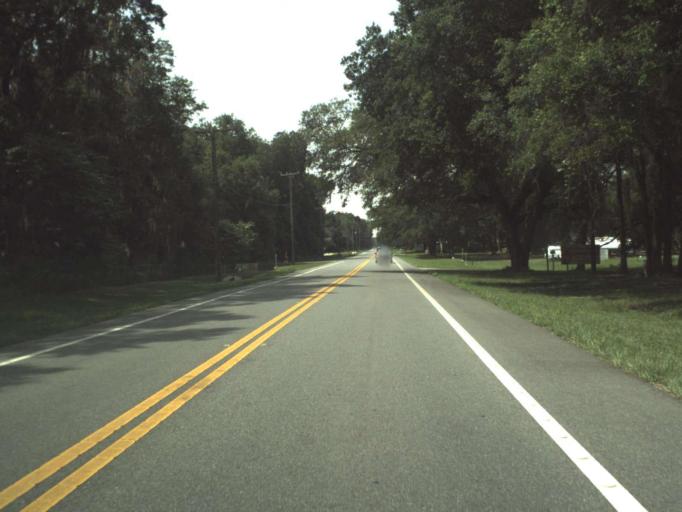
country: US
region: Florida
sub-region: Sumter County
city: Bushnell
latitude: 28.6954
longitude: -82.1043
